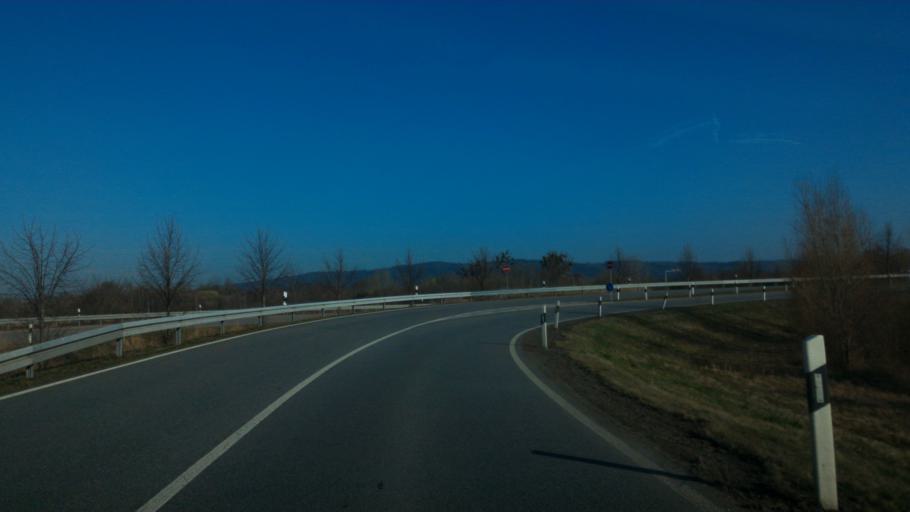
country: DE
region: Saxony
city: Pirna
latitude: 50.9678
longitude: 13.9143
